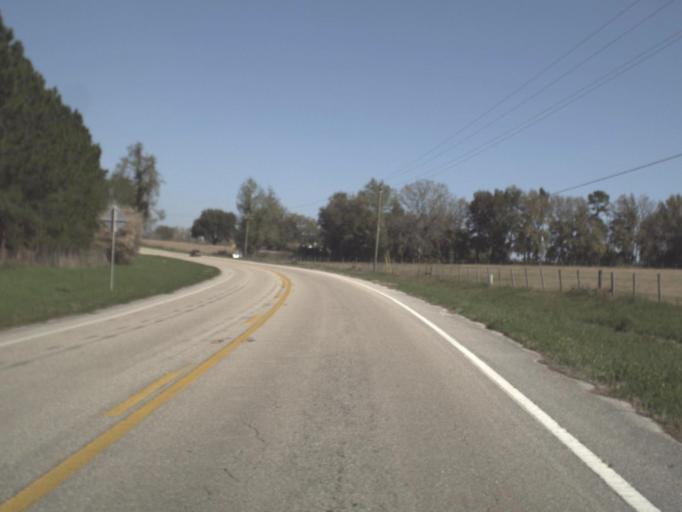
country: US
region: Florida
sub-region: Jefferson County
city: Monticello
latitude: 30.3667
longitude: -83.9901
